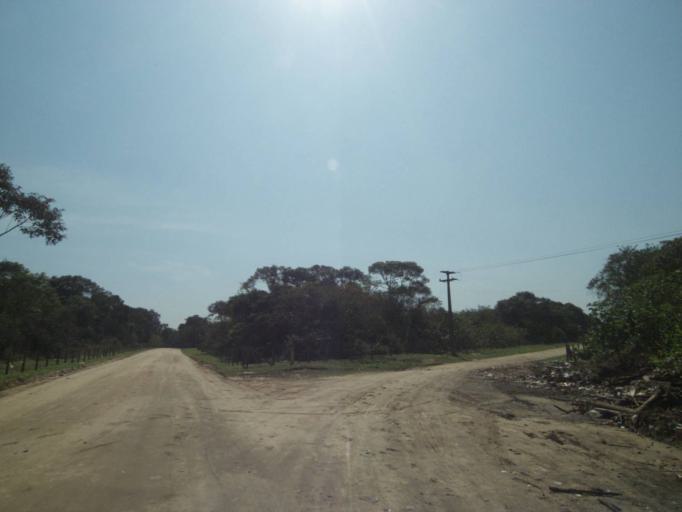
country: BR
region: Parana
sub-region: Paranagua
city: Paranagua
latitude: -25.5429
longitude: -48.5724
